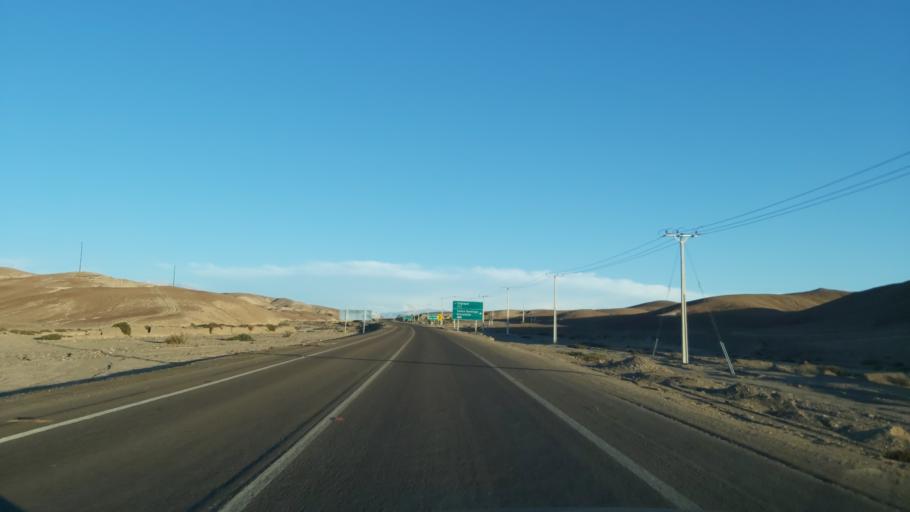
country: CL
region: Atacama
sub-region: Provincia de Chanaral
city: Diego de Almagro
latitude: -26.4157
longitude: -70.0315
